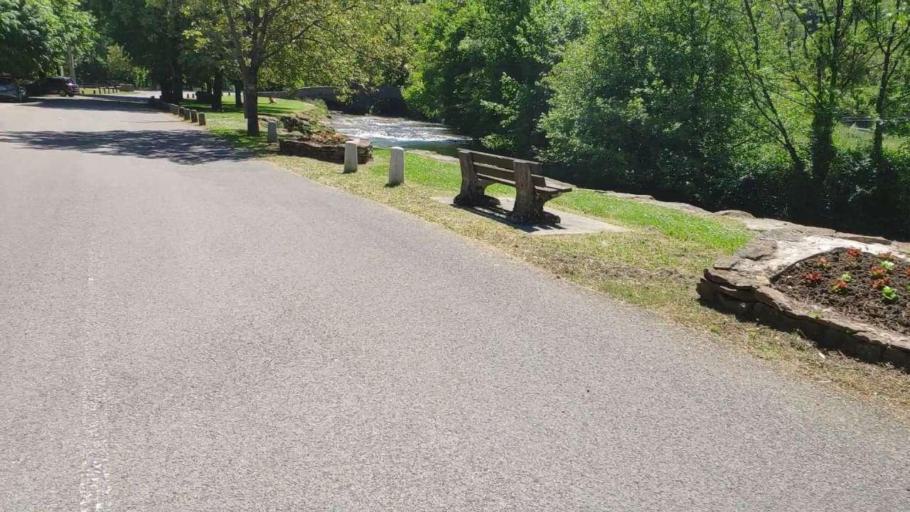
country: FR
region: Franche-Comte
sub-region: Departement du Jura
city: Perrigny
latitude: 46.7448
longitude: 5.6264
